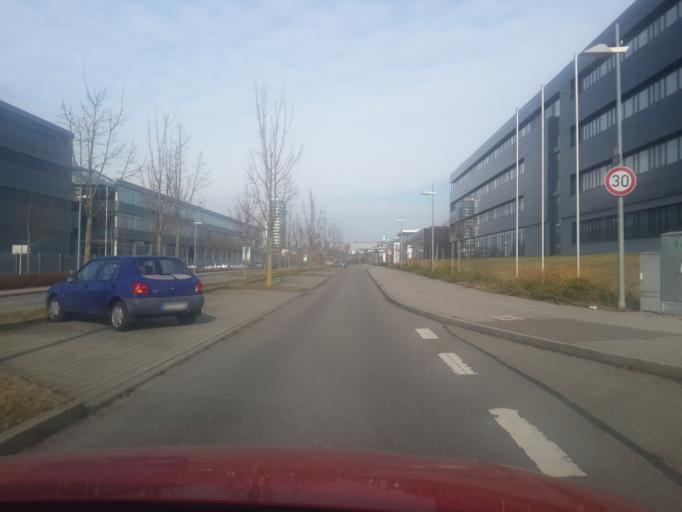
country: DE
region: Baden-Wuerttemberg
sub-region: Regierungsbezirk Stuttgart
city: Neckarsulm
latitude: 49.1758
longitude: 9.2297
